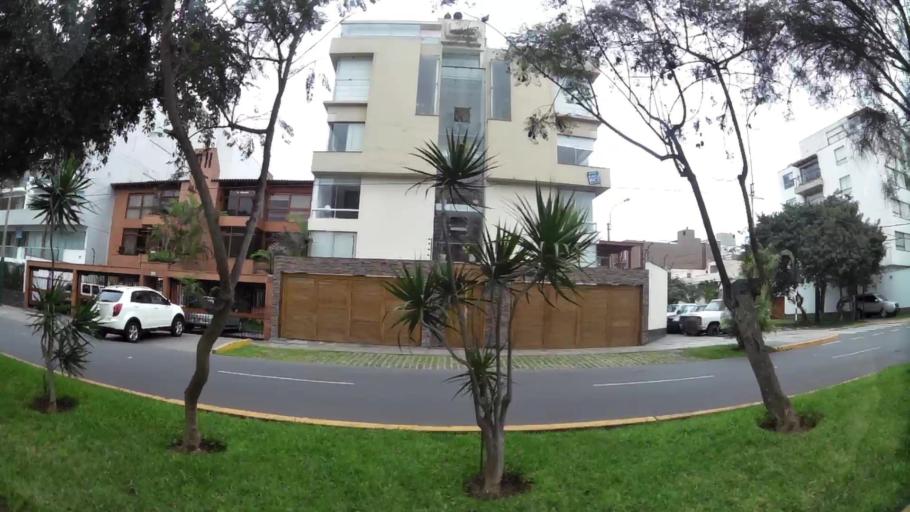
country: PE
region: Lima
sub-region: Lima
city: Surco
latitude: -12.1167
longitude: -76.9808
